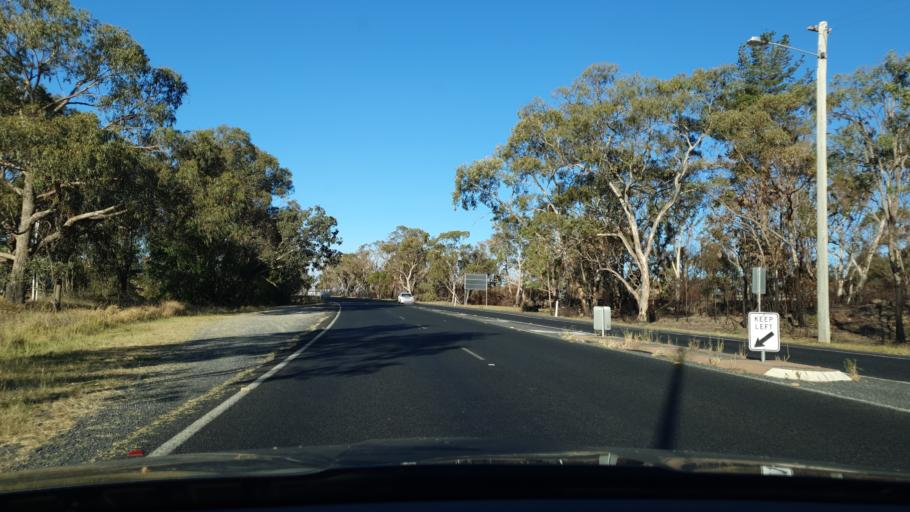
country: AU
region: Queensland
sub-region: Southern Downs
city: Stanthorpe
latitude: -28.6353
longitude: 151.9515
